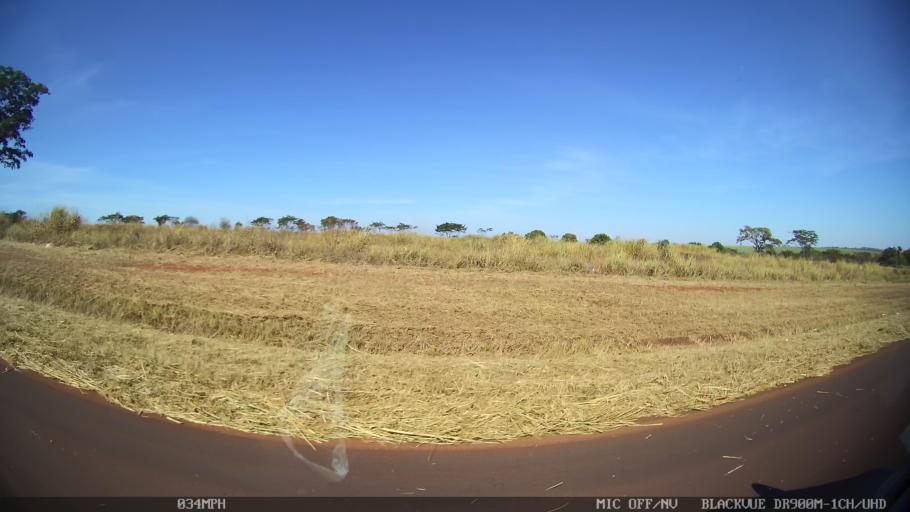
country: BR
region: Sao Paulo
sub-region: Barretos
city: Barretos
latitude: -20.4483
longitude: -48.4519
